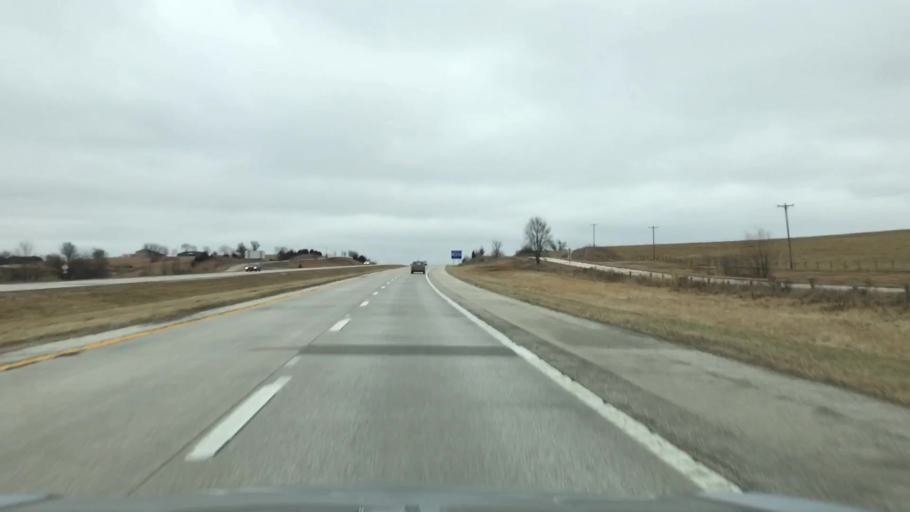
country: US
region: Missouri
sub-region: Linn County
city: Marceline
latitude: 39.7608
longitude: -92.9597
